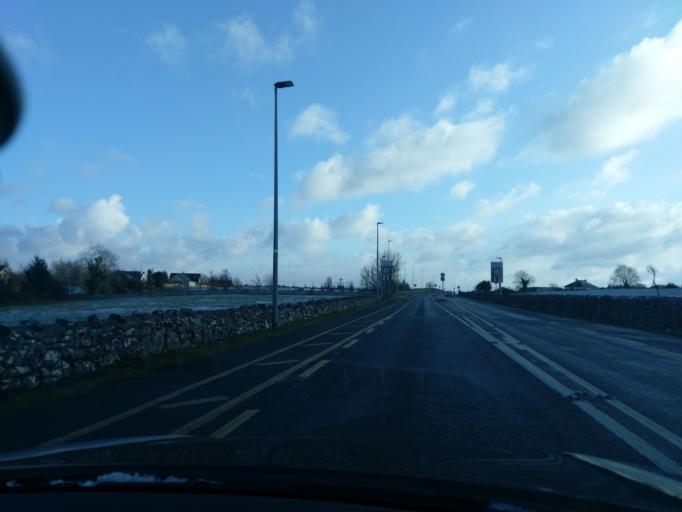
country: IE
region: Connaught
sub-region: County Galway
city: Gort
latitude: 53.1455
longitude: -8.8045
